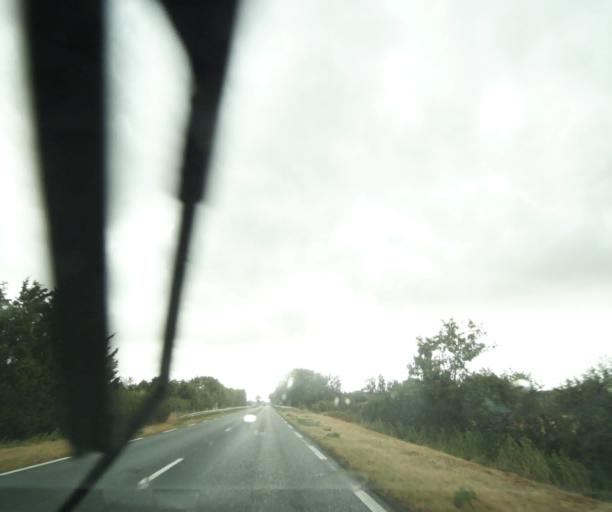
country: FR
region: Pays de la Loire
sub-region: Departement de la Vendee
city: Sainte-Foy
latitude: 46.4774
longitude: -1.6734
